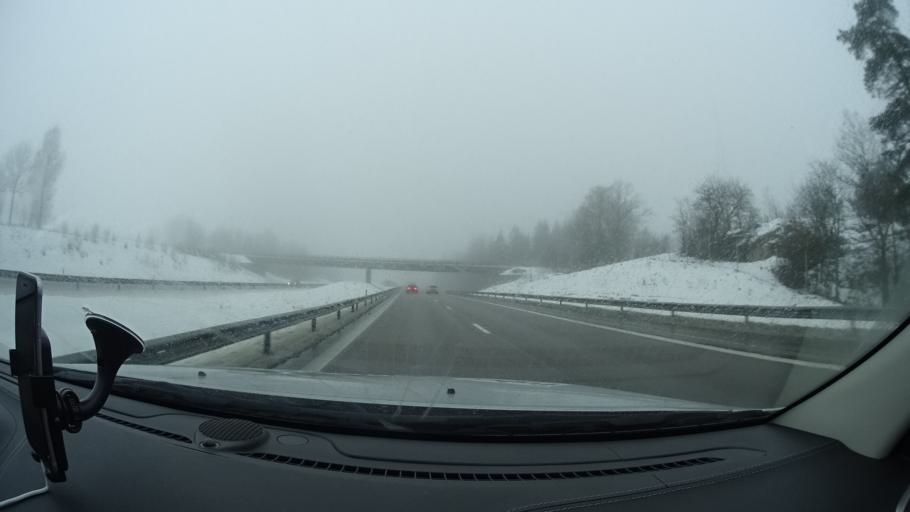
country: SE
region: OEstergoetland
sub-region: Mjolby Kommun
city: Mjolby
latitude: 58.3108
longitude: 15.0199
